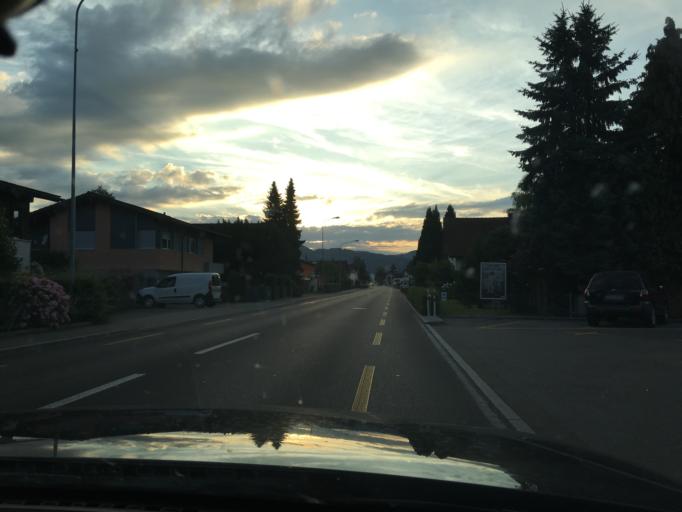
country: CH
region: Saint Gallen
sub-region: Wahlkreis Rheintal
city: Diepoldsau
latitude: 47.3816
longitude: 9.6634
